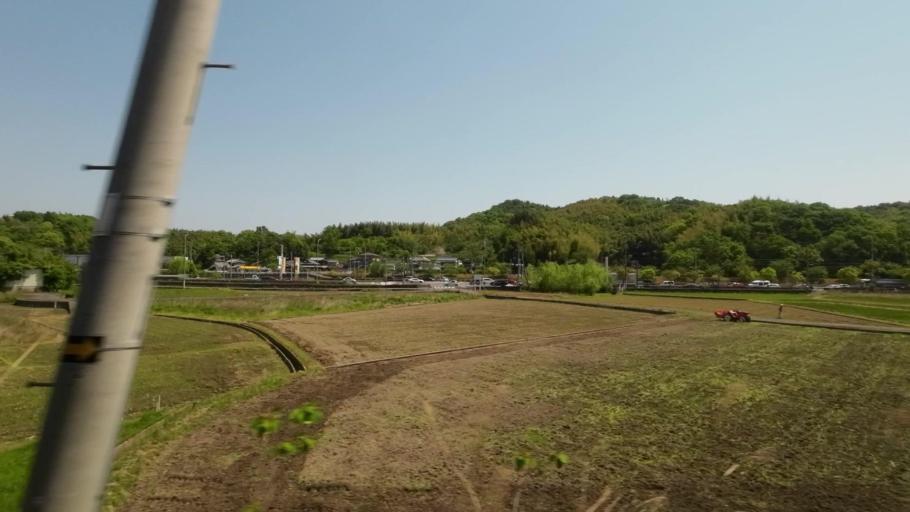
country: JP
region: Ehime
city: Saijo
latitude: 33.9997
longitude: 133.0390
